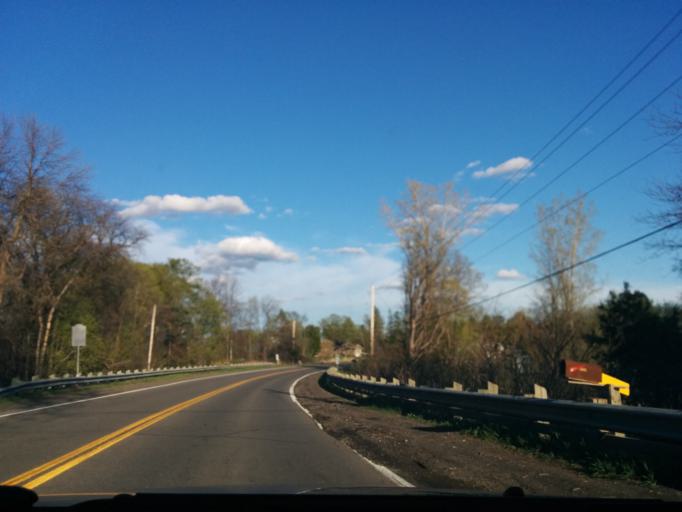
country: CA
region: Ontario
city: Bells Corners
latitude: 45.2334
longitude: -75.6746
